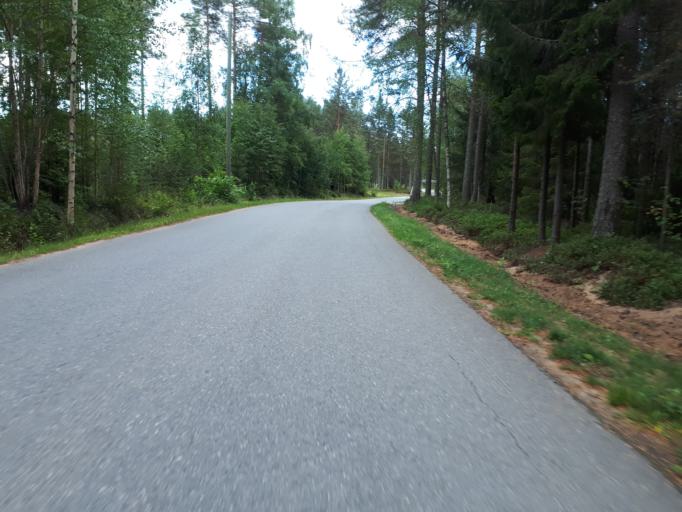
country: FI
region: Northern Ostrobothnia
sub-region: Oulunkaari
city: Ii
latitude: 65.3270
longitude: 25.3921
